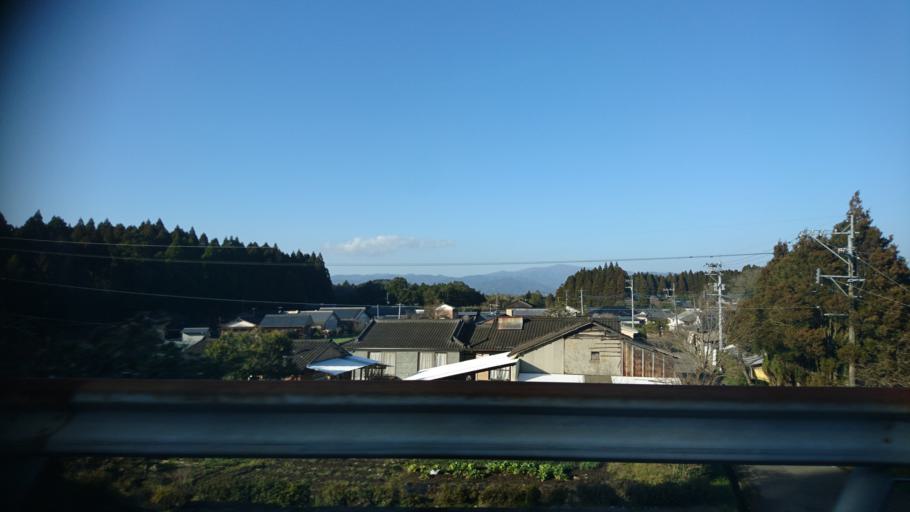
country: JP
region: Miyazaki
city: Kobayashi
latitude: 31.9970
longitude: 130.9010
